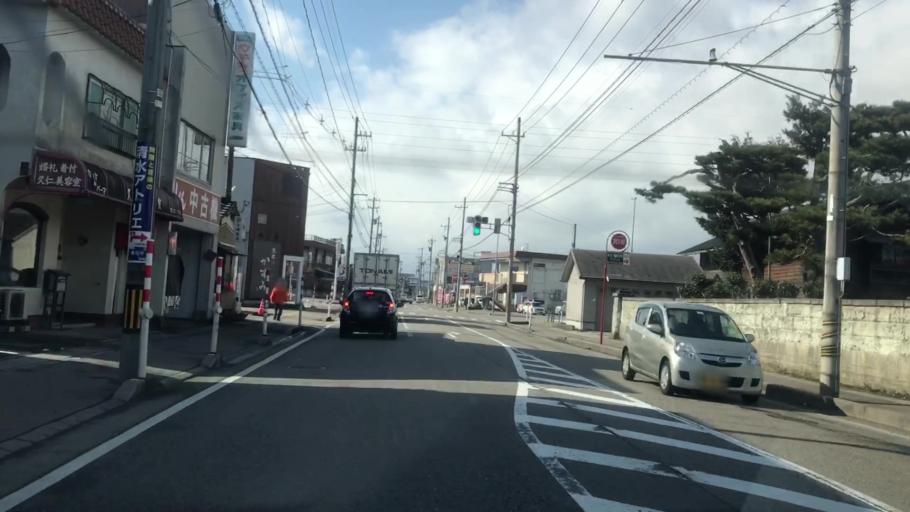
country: JP
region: Toyama
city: Takaoka
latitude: 36.7370
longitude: 137.0336
